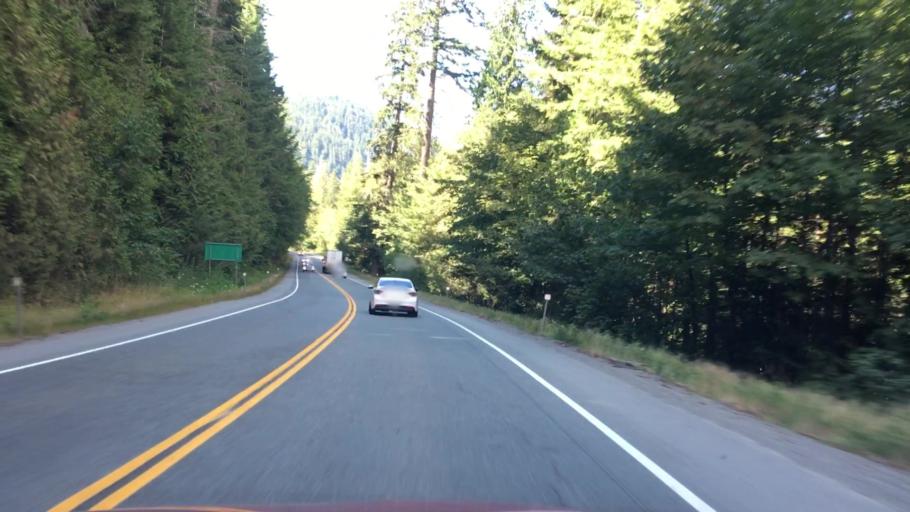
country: CA
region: British Columbia
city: Port Alberni
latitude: 49.2560
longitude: -124.6660
